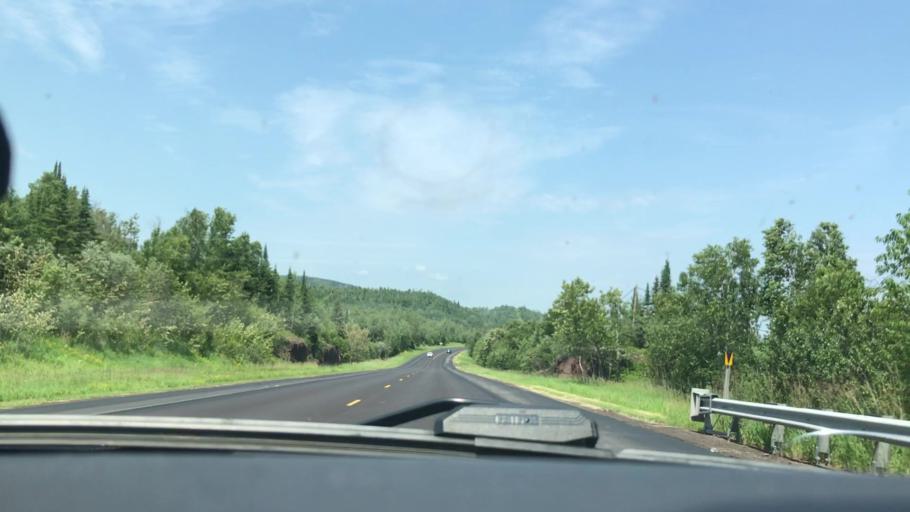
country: US
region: Minnesota
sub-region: Lake County
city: Silver Bay
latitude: 47.3514
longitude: -91.1832
